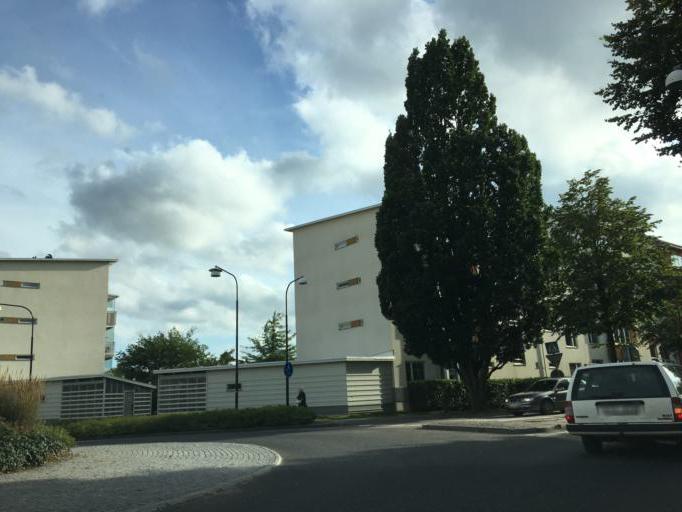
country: SE
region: Uppsala
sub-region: Enkopings Kommun
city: Enkoping
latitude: 59.6355
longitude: 17.0845
